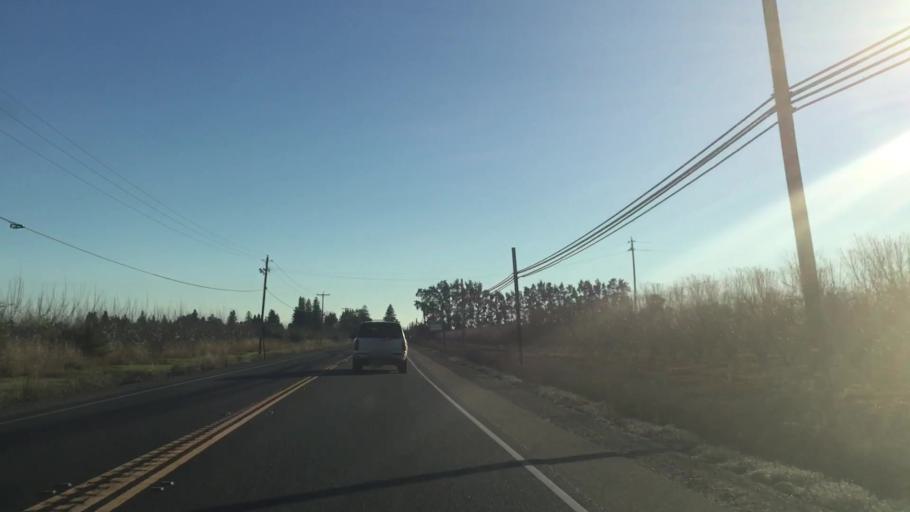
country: US
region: California
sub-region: Yuba County
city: Marysville
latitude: 39.1967
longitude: -121.5950
